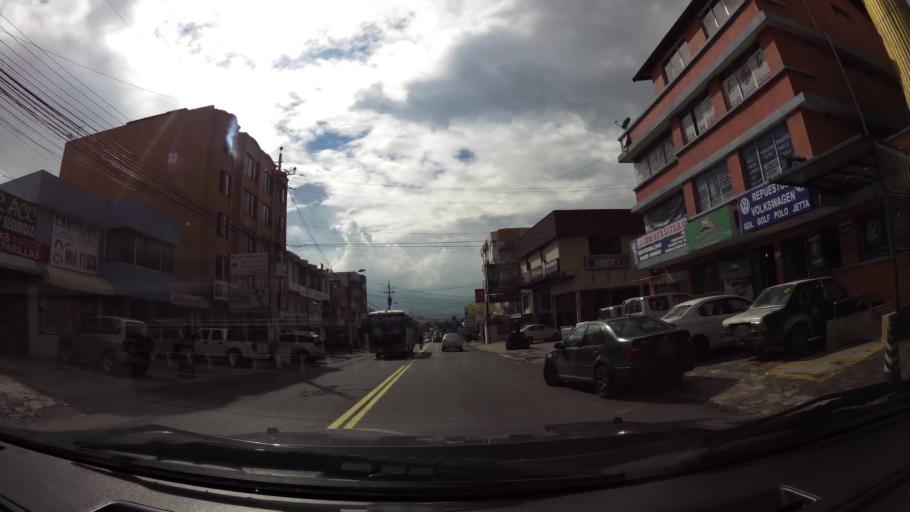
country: EC
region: Pichincha
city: Sangolqui
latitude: -0.3054
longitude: -78.4556
